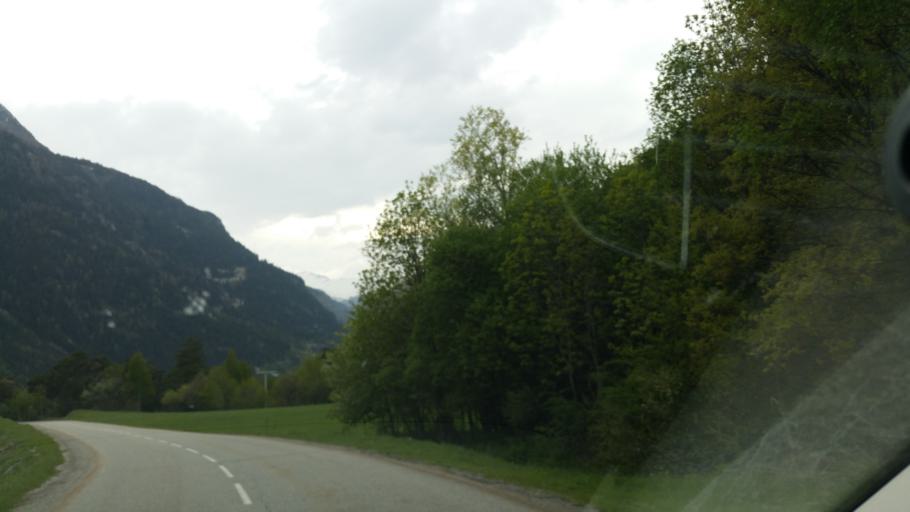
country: FR
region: Rhone-Alpes
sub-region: Departement de la Savoie
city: Modane
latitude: 45.2043
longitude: 6.6063
